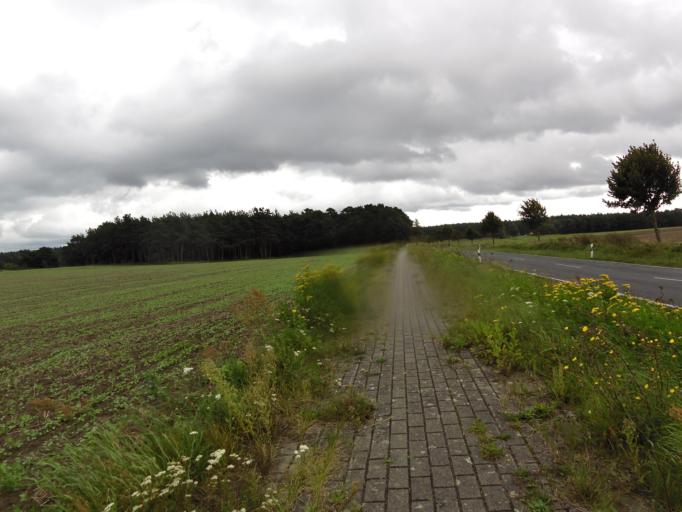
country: DE
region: Saxony-Anhalt
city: Hohenberg-Krusemark
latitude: 52.7015
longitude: 11.9719
